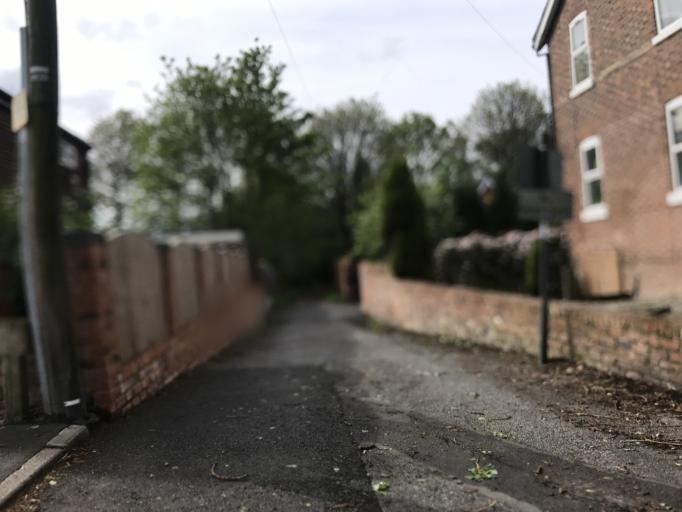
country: GB
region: England
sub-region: Manchester
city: Heaton Chapel
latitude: 53.4147
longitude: -2.1763
